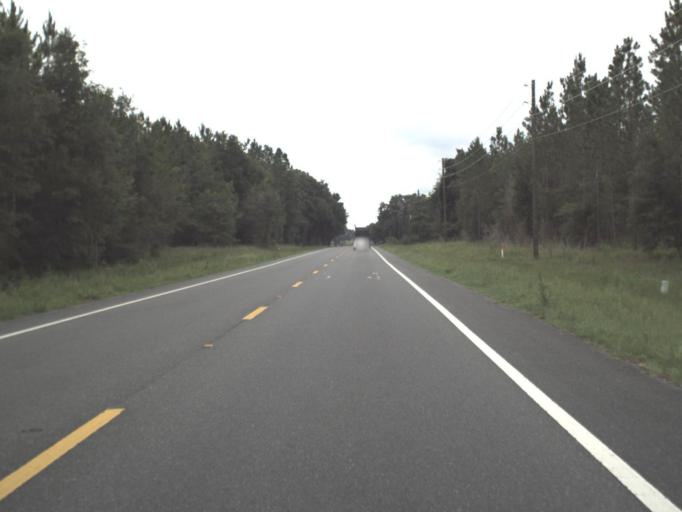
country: US
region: Florida
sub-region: Levy County
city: Williston
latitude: 29.2731
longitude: -82.4430
